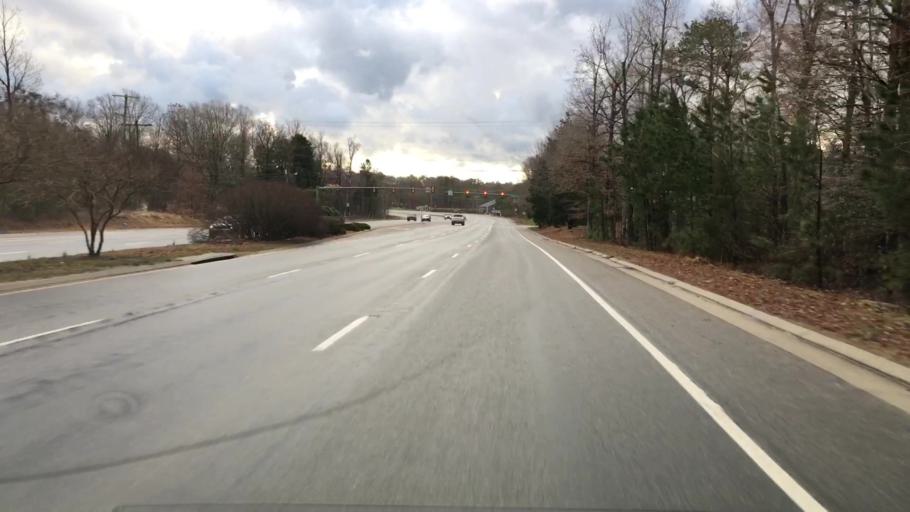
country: US
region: Virginia
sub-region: Chesterfield County
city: Bon Air
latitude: 37.4976
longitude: -77.6070
